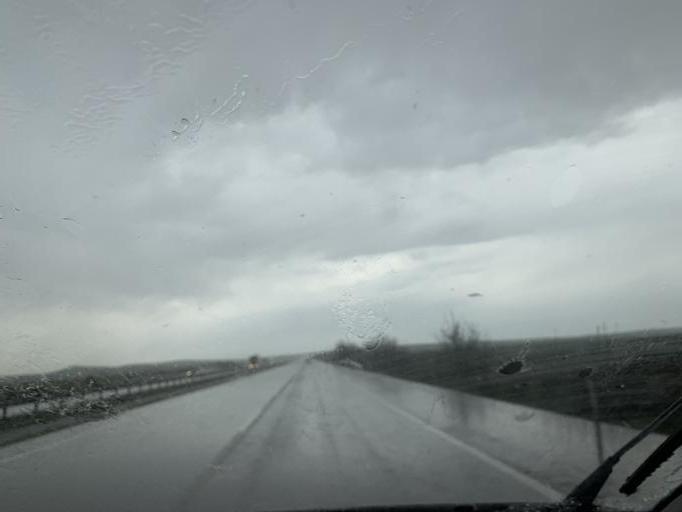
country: TR
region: Eskisehir
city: Gunyuzu
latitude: 39.5749
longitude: 31.8741
